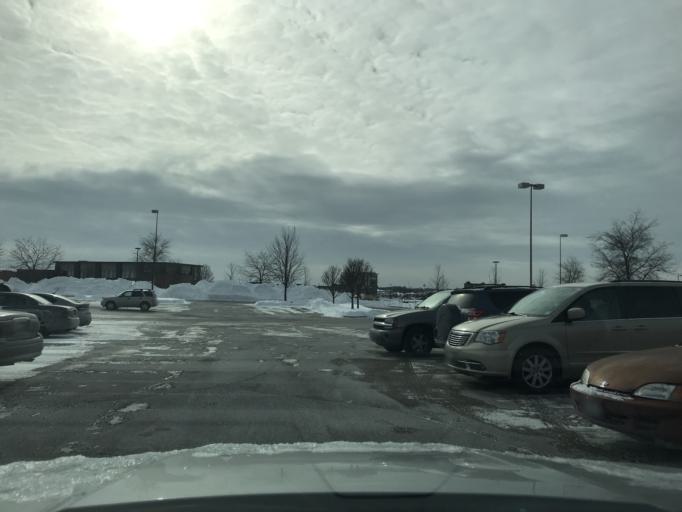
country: US
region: Wisconsin
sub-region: Dane County
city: Sun Prairie
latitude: 43.1705
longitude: -89.2686
